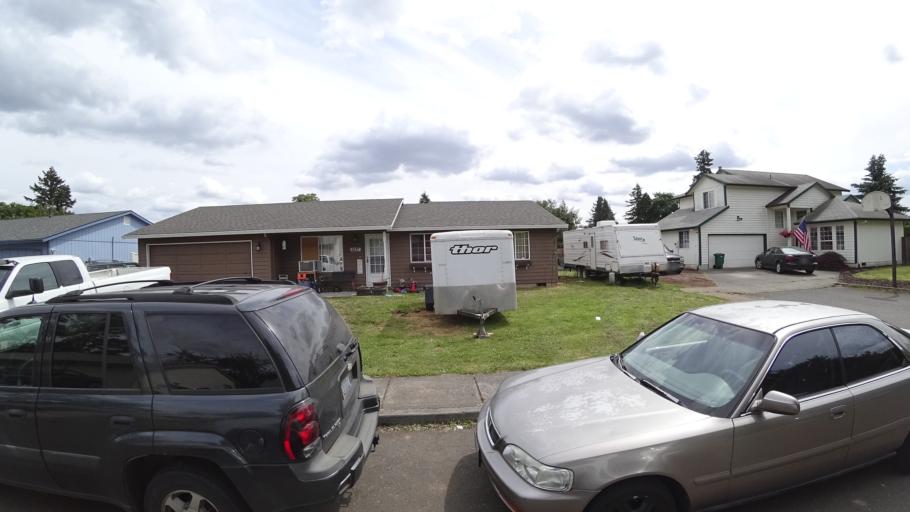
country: US
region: Oregon
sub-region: Multnomah County
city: Lents
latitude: 45.4843
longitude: -122.5502
